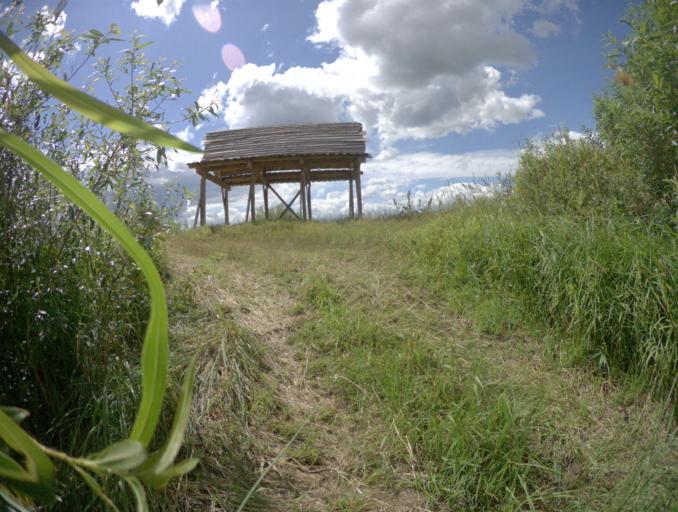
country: RU
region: Vladimir
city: Orgtrud
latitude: 56.3053
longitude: 40.6362
